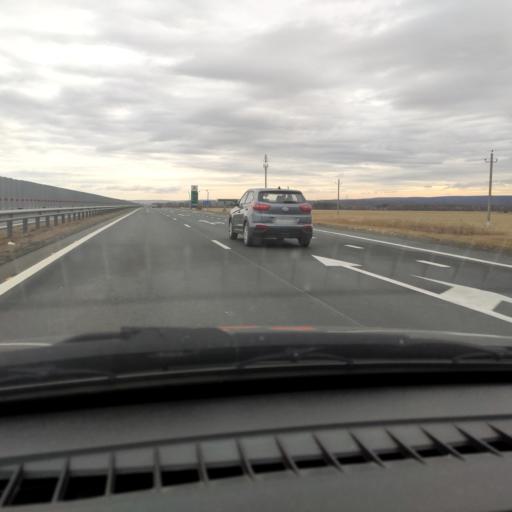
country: RU
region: Samara
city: Bereza
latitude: 53.4726
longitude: 50.1661
